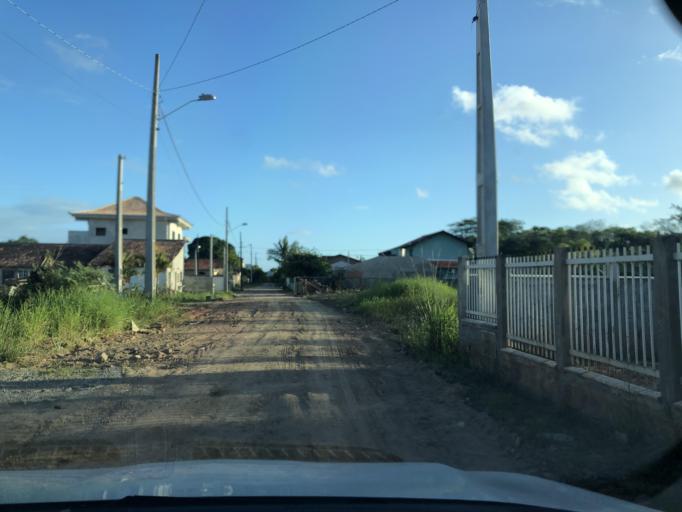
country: BR
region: Santa Catarina
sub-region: Sao Francisco Do Sul
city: Sao Francisco do Sul
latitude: -26.2248
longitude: -48.5265
